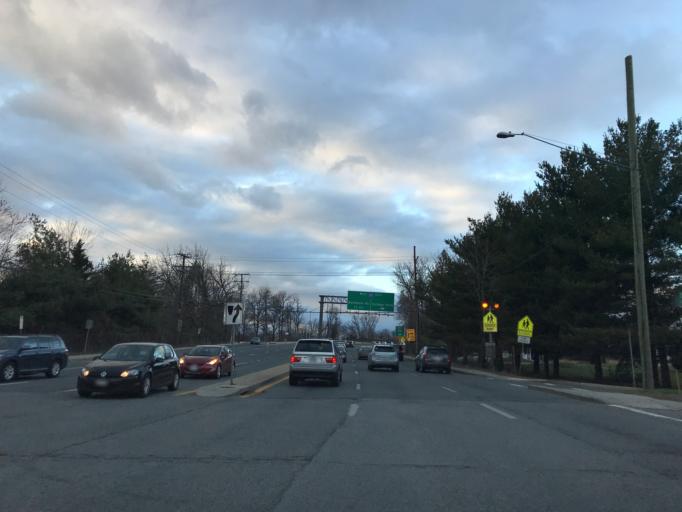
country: US
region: Maryland
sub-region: Montgomery County
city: Four Corners
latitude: 39.0131
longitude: -77.0166
